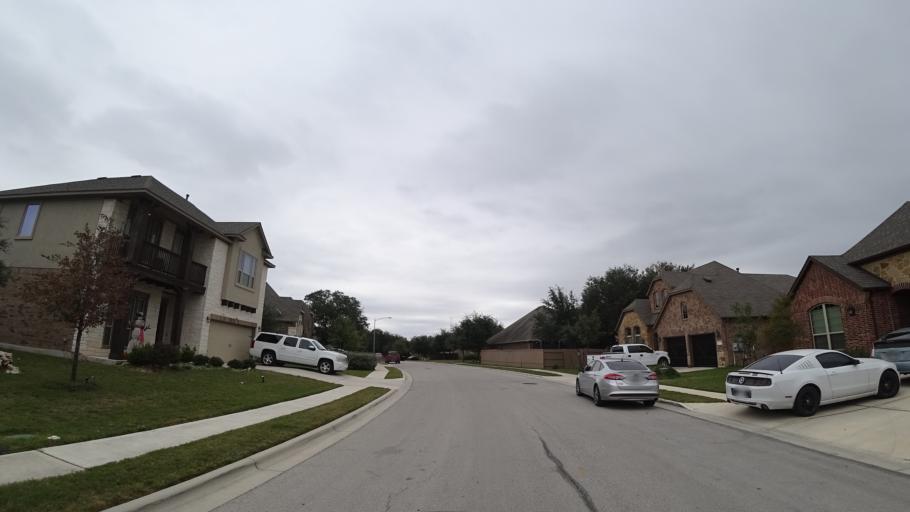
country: US
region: Texas
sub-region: Travis County
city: Manchaca
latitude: 30.1457
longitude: -97.8519
